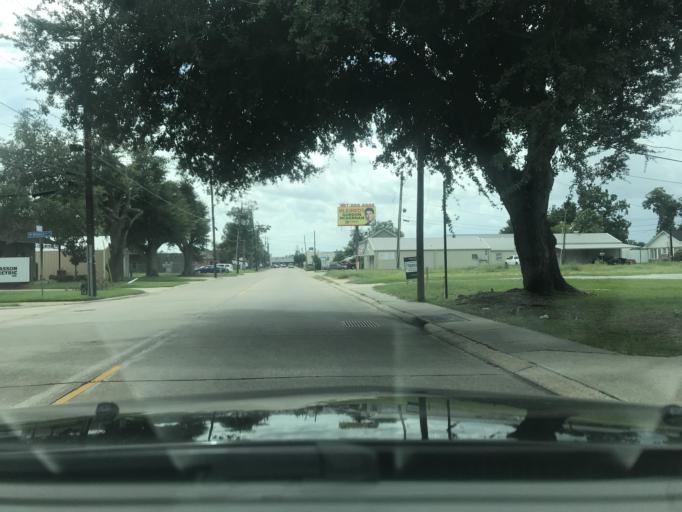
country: US
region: Louisiana
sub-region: Calcasieu Parish
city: Lake Charles
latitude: 30.2034
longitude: -93.2153
